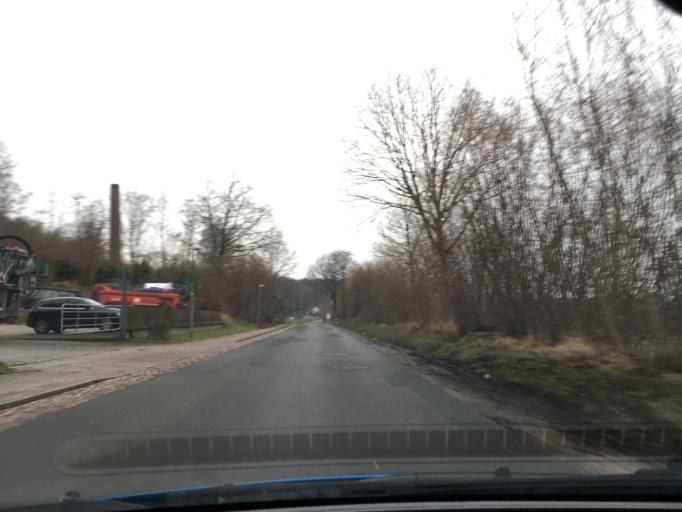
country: DE
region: Schleswig-Holstein
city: Buchhorst
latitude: 53.3790
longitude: 10.5764
